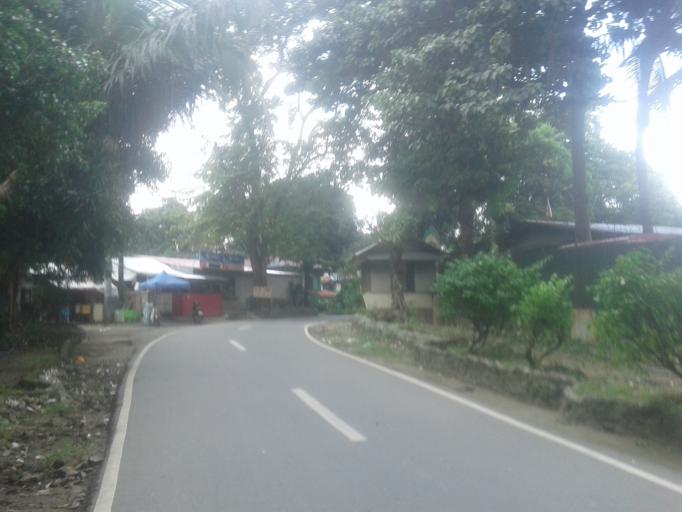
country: PH
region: Metro Manila
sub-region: Mandaluyong
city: Mandaluyong City
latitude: 14.5833
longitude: 121.0398
